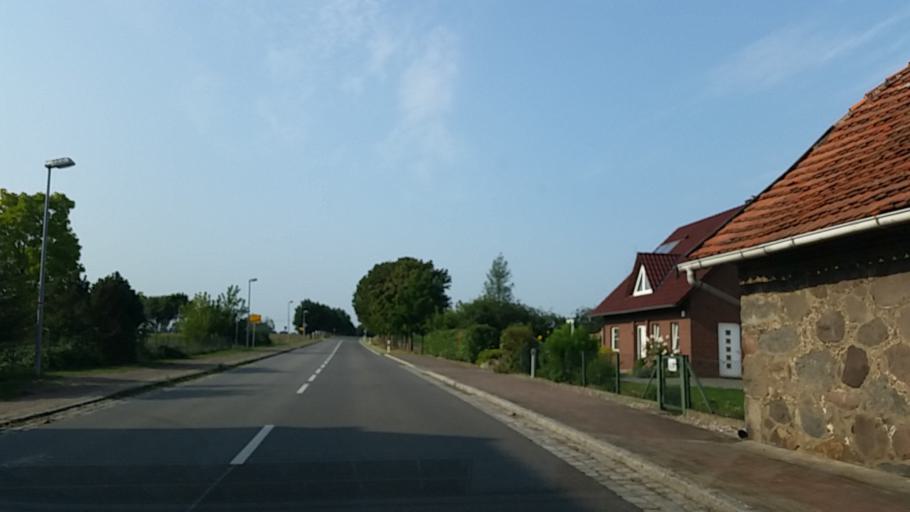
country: DE
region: Mecklenburg-Vorpommern
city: Hagenow
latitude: 53.4051
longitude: 11.1165
